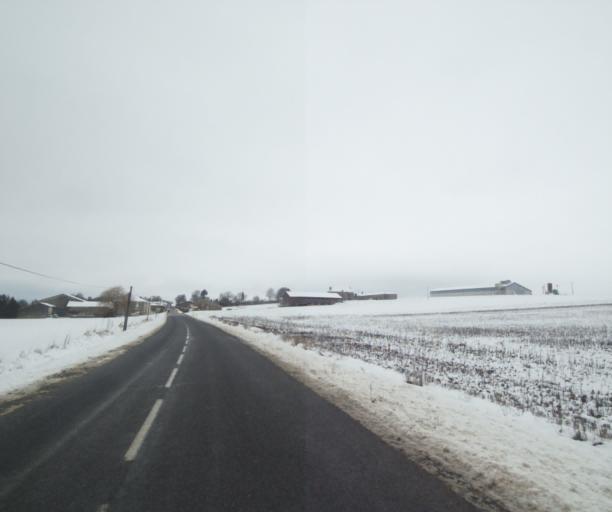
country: FR
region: Champagne-Ardenne
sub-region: Departement de la Haute-Marne
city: Wassy
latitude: 48.4513
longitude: 4.9607
